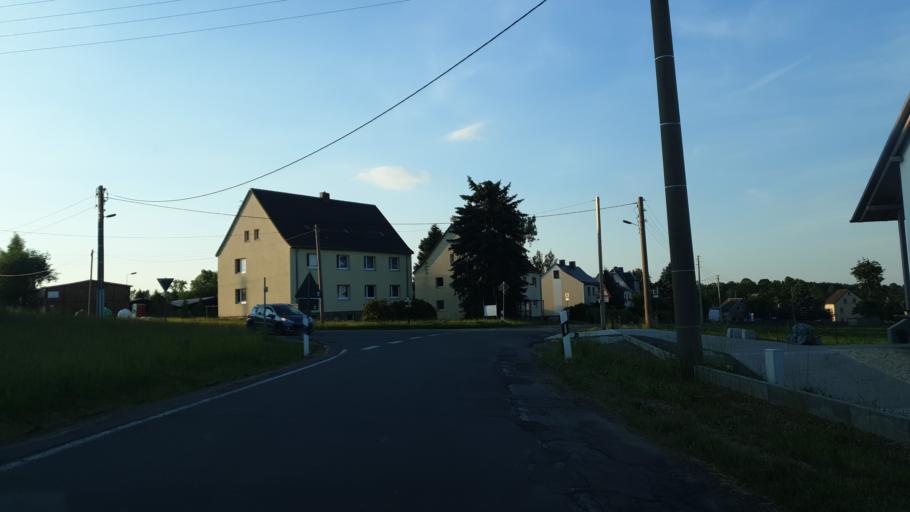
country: DE
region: Saxony
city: Stollberg
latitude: 50.6823
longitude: 12.7398
